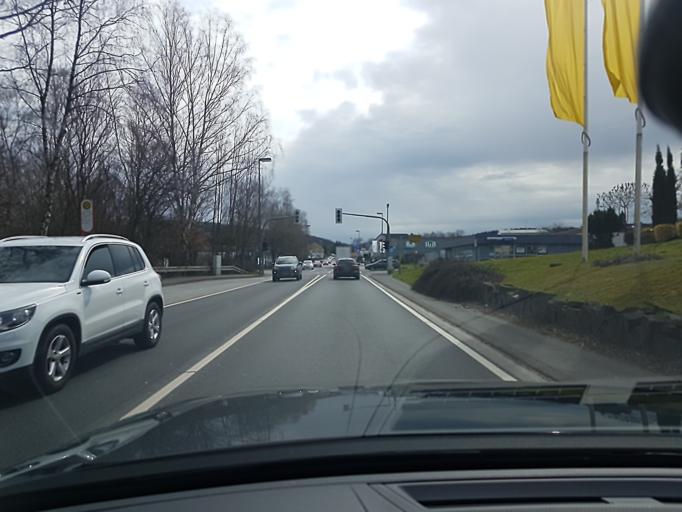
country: DE
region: North Rhine-Westphalia
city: Iserlohn
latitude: 51.4069
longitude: 7.6944
